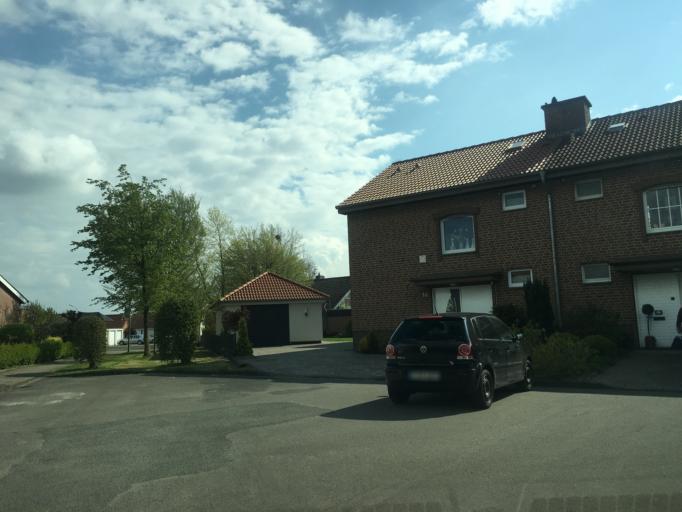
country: DE
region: North Rhine-Westphalia
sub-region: Regierungsbezirk Munster
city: Steinfurt
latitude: 52.1367
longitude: 7.3269
